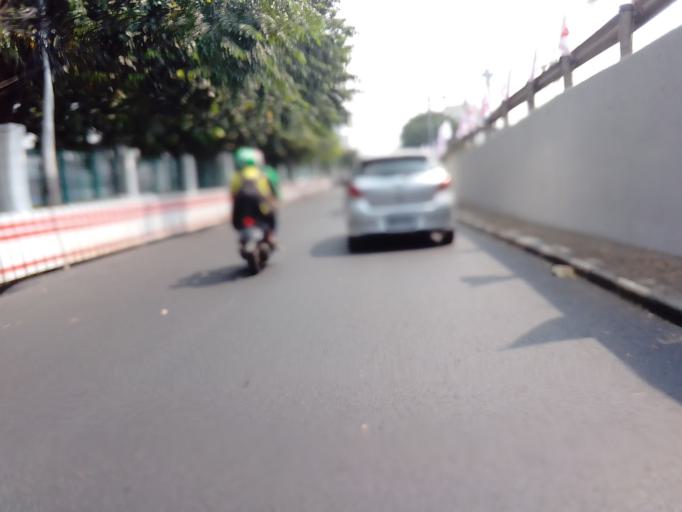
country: ID
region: Jakarta Raya
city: Jakarta
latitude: -6.2128
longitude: 106.8061
